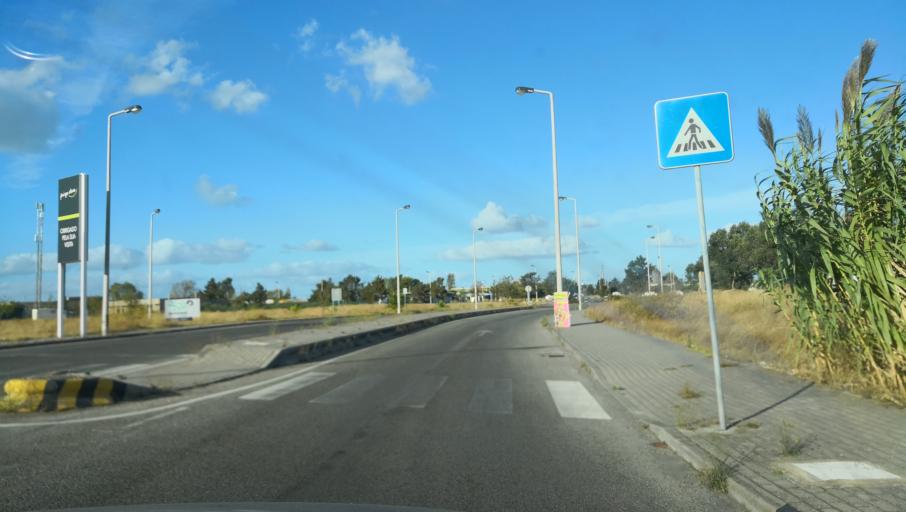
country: PT
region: Setubal
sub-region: Barreiro
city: Barreiro
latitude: 38.6694
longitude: -9.0570
